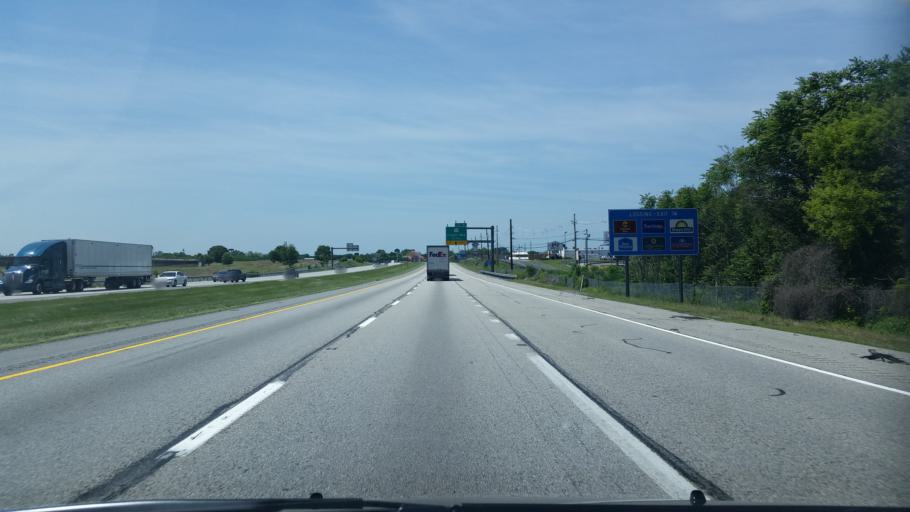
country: US
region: Pennsylvania
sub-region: Franklin County
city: Guilford
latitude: 39.9383
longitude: -77.6265
